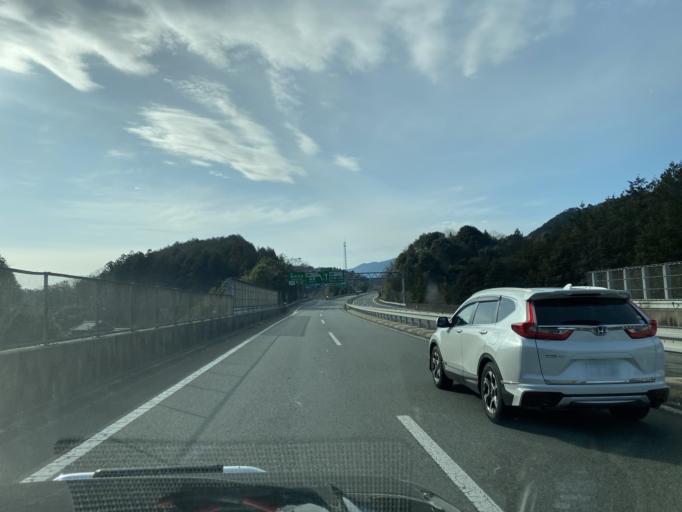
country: JP
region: Mie
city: Ise
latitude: 34.4624
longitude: 136.5143
